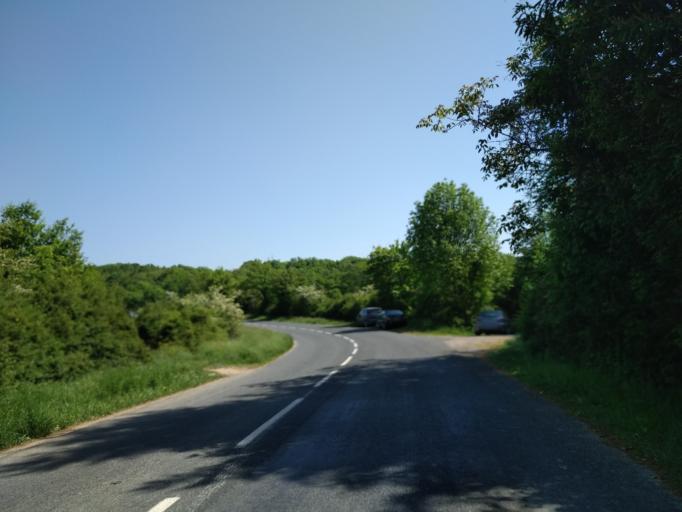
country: FR
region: Rhone-Alpes
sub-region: Departement du Rhone
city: Fontaines-sur-Saone
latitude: 45.8285
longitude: 4.8111
